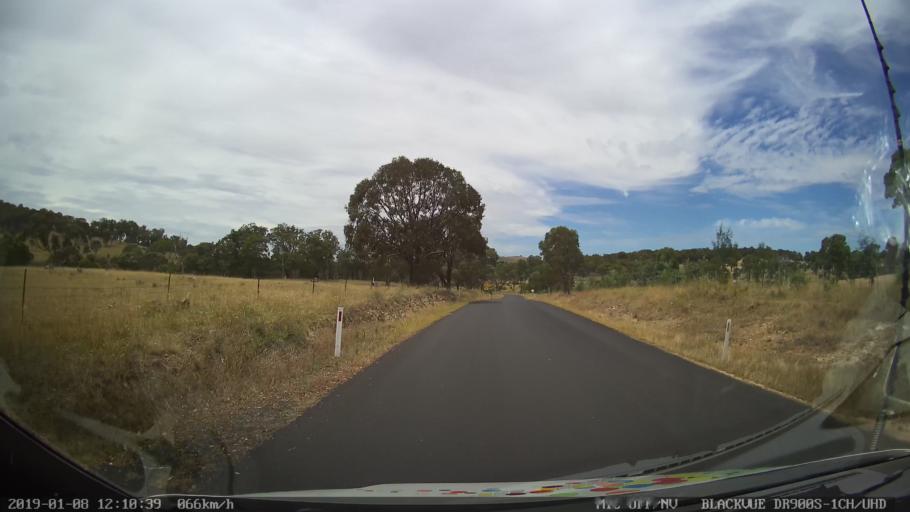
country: AU
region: New South Wales
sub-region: Armidale Dumaresq
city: Armidale
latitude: -30.4450
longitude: 151.5900
